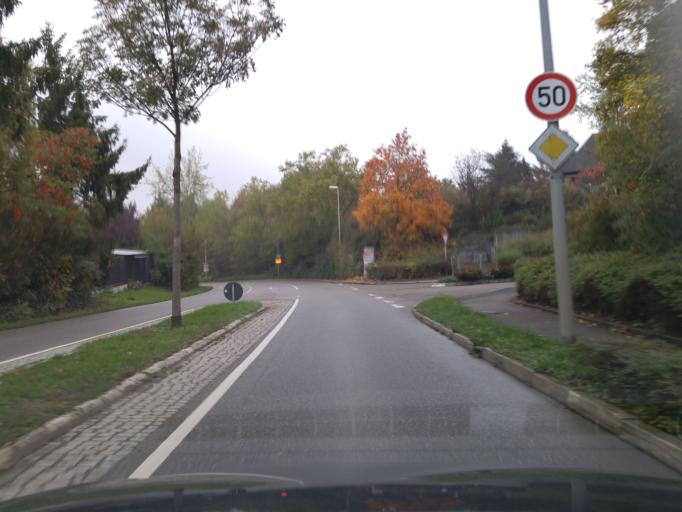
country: DE
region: Baden-Wuerttemberg
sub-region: Regierungsbezirk Stuttgart
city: Bad Wimpfen
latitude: 49.2236
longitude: 9.1601
